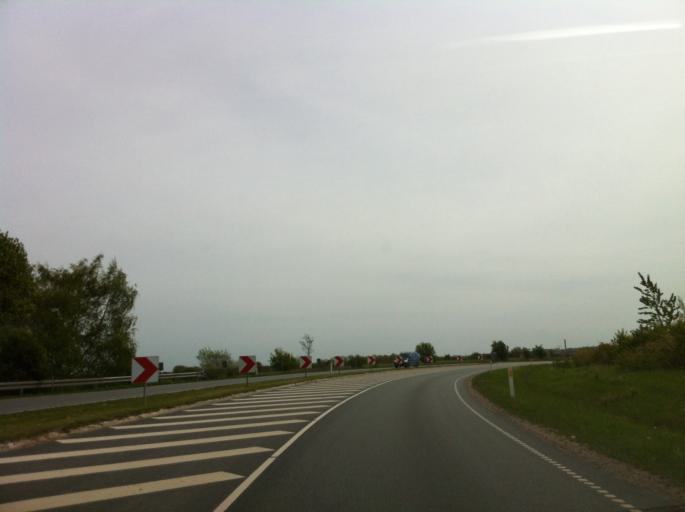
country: DK
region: Zealand
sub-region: Roskilde Kommune
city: Roskilde
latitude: 55.6650
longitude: 12.1148
